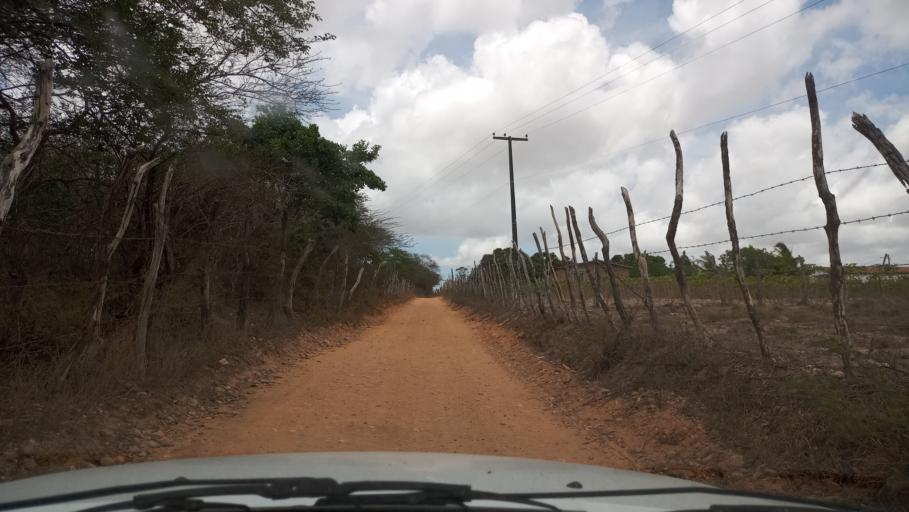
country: BR
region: Rio Grande do Norte
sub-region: Goianinha
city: Goianinha
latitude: -6.3002
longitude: -35.2758
